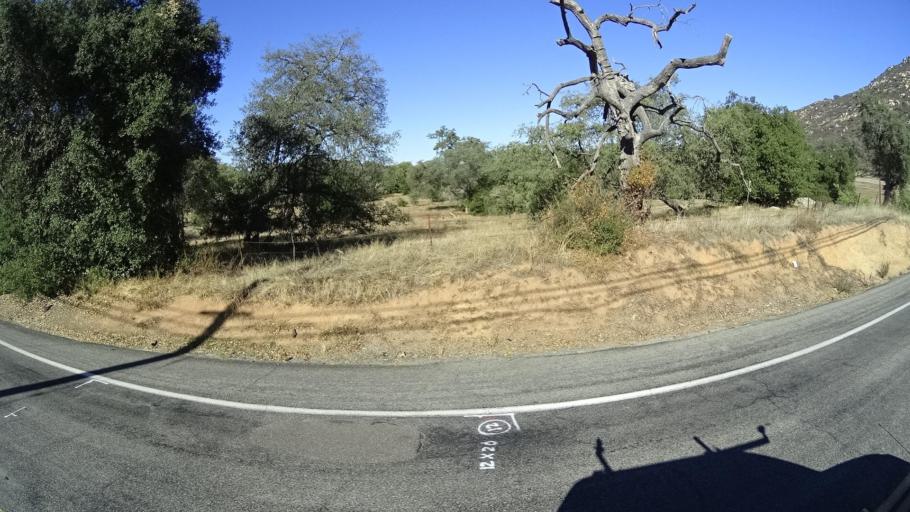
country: US
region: California
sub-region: San Diego County
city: Alpine
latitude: 32.7111
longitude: -116.7472
